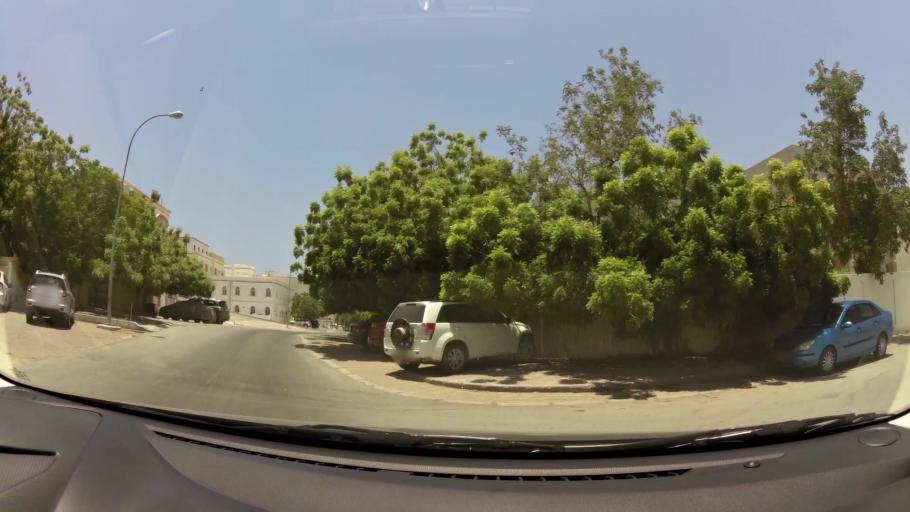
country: OM
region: Muhafazat Masqat
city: Muscat
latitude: 23.6257
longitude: 58.5395
